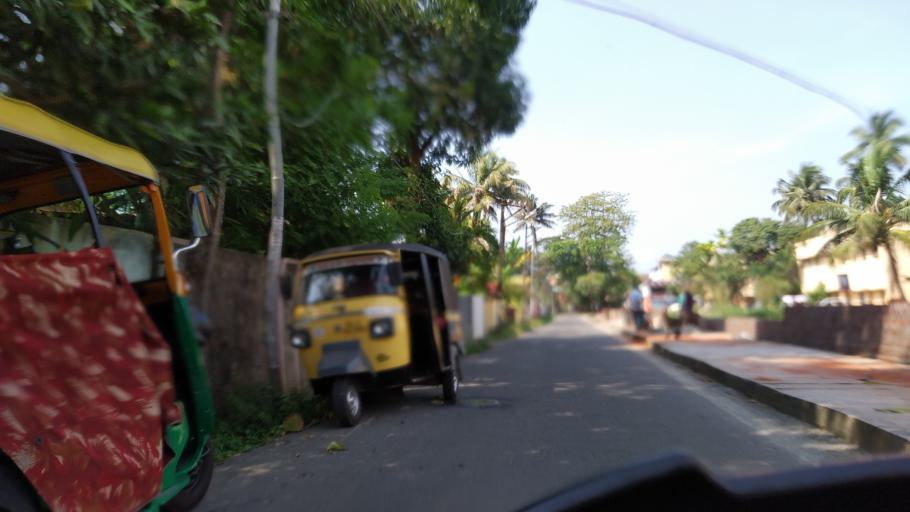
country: IN
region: Kerala
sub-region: Ernakulam
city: Cochin
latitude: 9.9723
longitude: 76.2896
